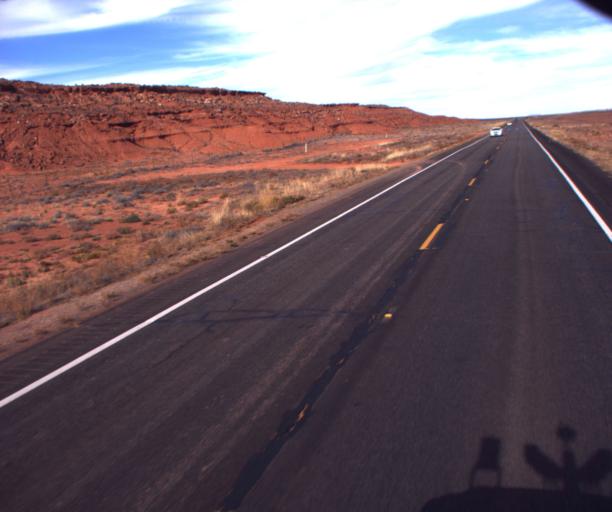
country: US
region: Arizona
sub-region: Navajo County
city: Kayenta
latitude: 36.9072
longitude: -109.7860
